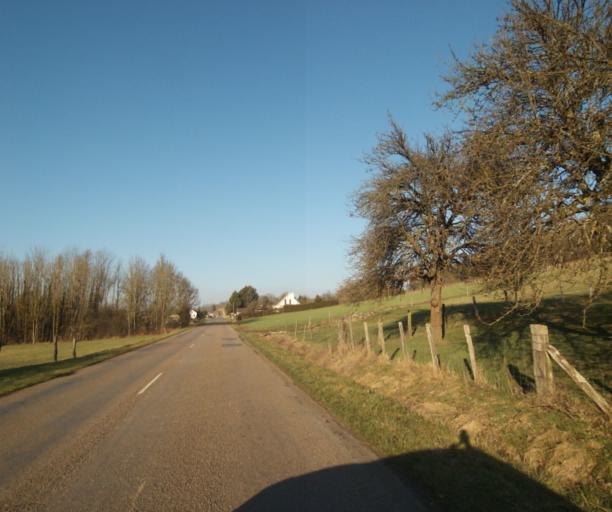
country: FR
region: Champagne-Ardenne
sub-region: Departement de la Haute-Marne
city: Chevillon
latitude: 48.5347
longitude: 5.1063
